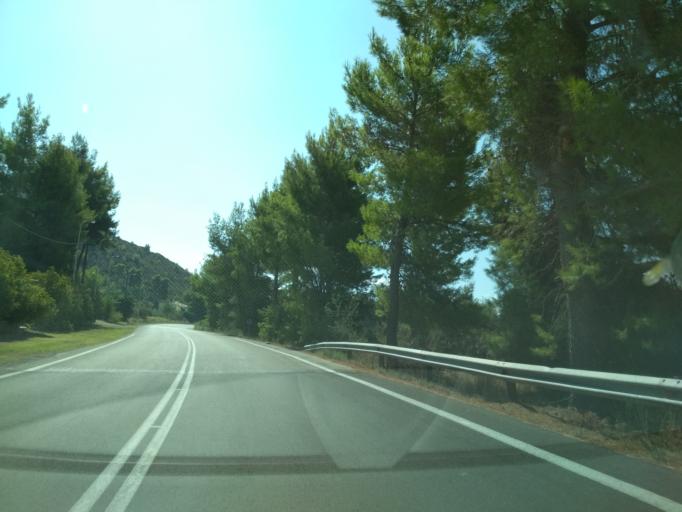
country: GR
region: Central Greece
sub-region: Nomos Evvoias
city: Roviai
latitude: 38.8222
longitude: 23.2284
